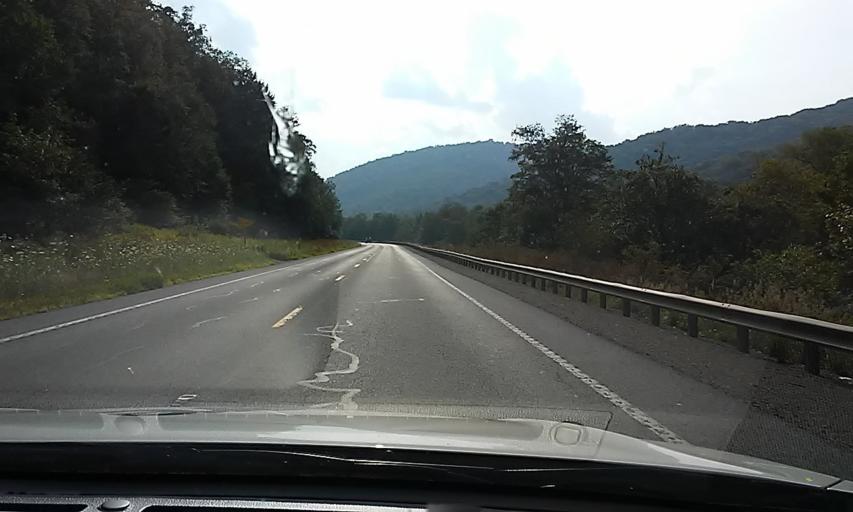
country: US
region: Pennsylvania
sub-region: Potter County
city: Galeton
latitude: 41.7889
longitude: -77.7852
